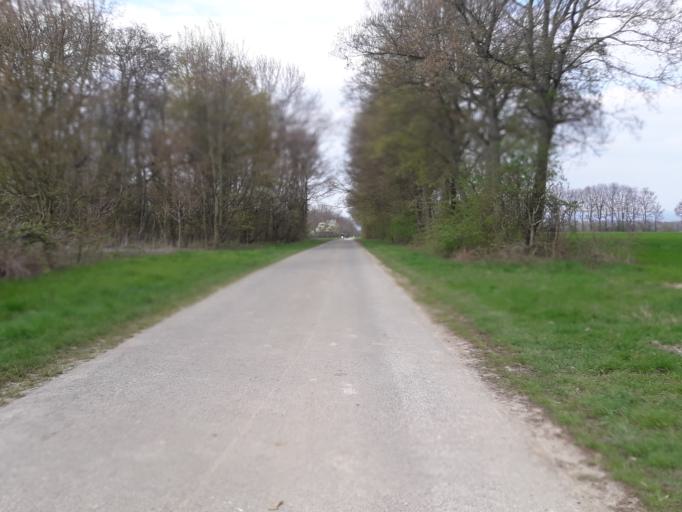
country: DE
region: North Rhine-Westphalia
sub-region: Regierungsbezirk Detmold
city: Paderborn
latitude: 51.6884
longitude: 8.7658
